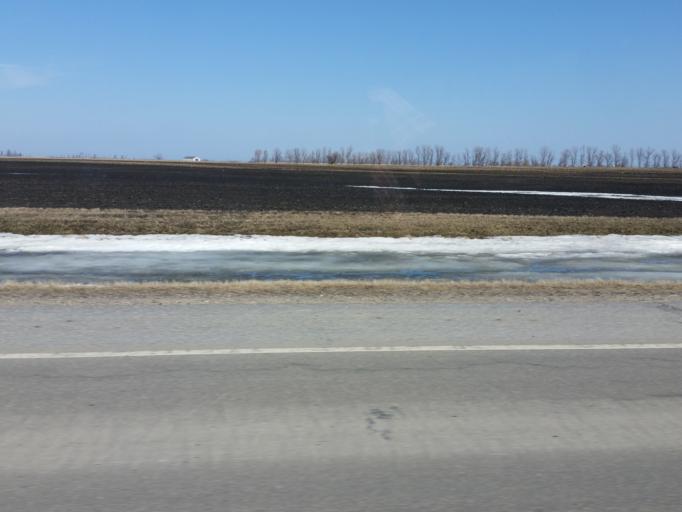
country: US
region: North Dakota
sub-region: Walsh County
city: Grafton
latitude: 48.2976
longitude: -97.3749
